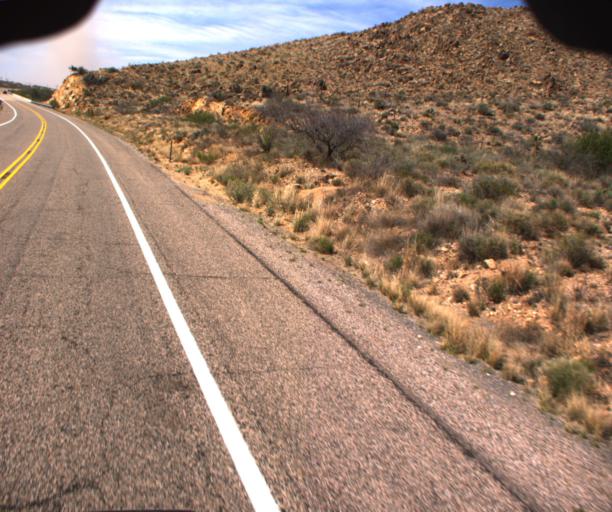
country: US
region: Arizona
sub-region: Mohave County
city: New Kingman-Butler
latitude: 35.3782
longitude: -113.7264
